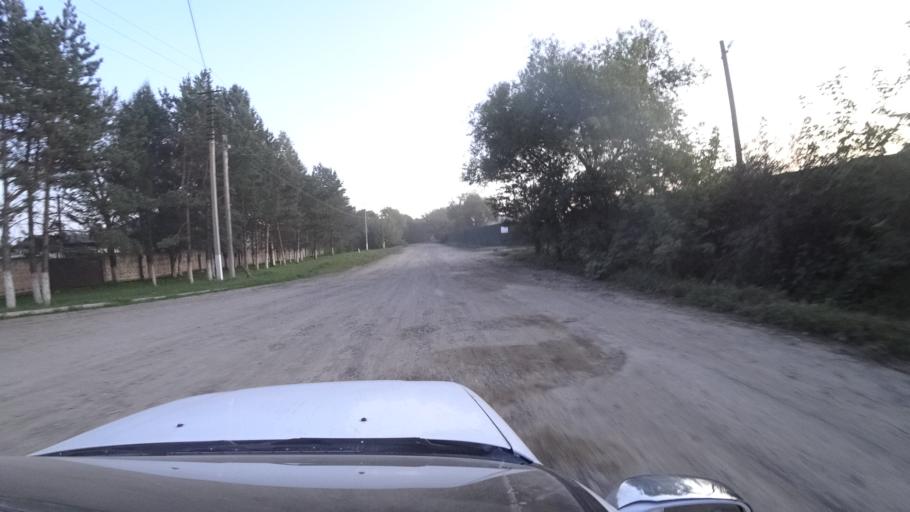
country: RU
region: Primorskiy
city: Dal'nerechensk
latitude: 45.9360
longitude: 133.7594
